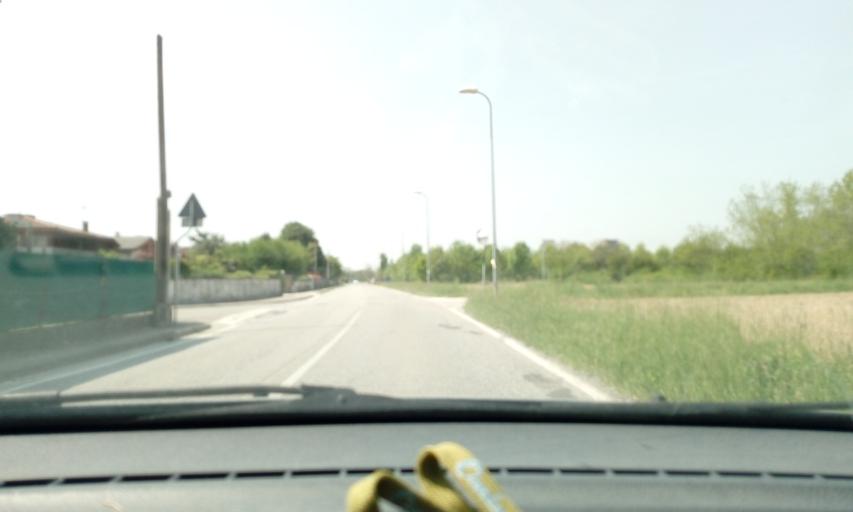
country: IT
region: Friuli Venezia Giulia
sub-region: Provincia di Udine
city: Pradamano
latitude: 46.0403
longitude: 13.3041
